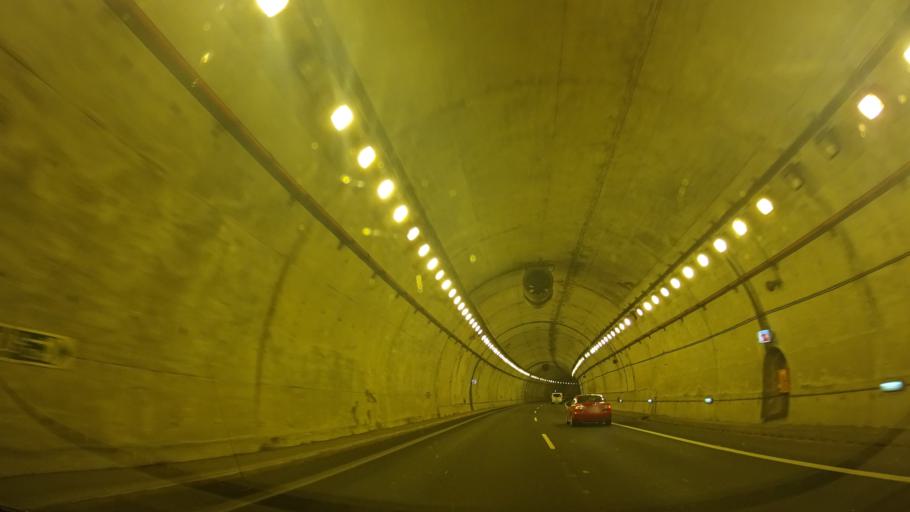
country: ES
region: Asturias
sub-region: Province of Asturias
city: Arriba
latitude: 43.5072
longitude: -5.5792
